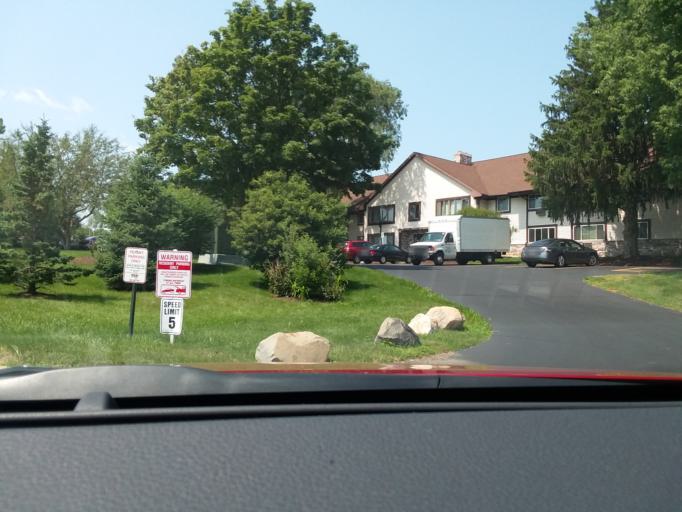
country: US
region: Wisconsin
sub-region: Dane County
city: Madison
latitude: 43.0256
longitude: -89.4100
